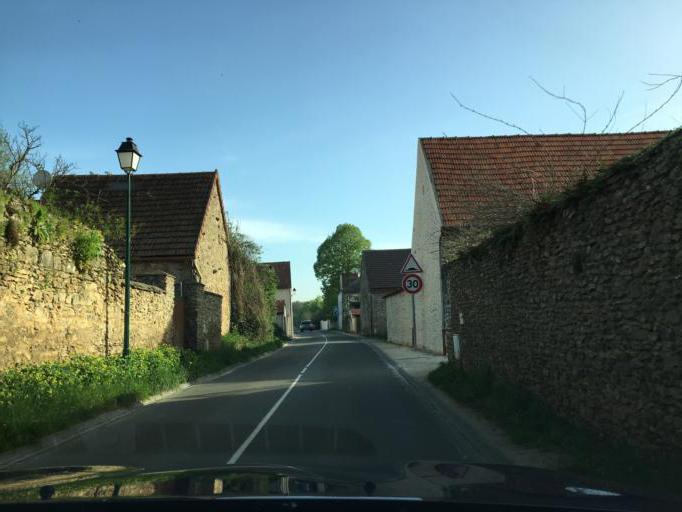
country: FR
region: Centre
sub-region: Departement d'Eure-et-Loir
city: Epernon
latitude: 48.6211
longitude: 1.6778
